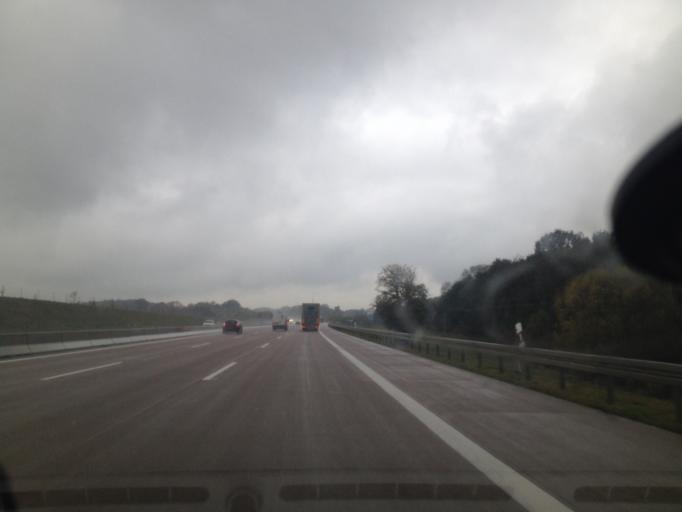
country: DE
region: Bavaria
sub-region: Swabia
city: Rettenbach
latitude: 48.4345
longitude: 10.3360
